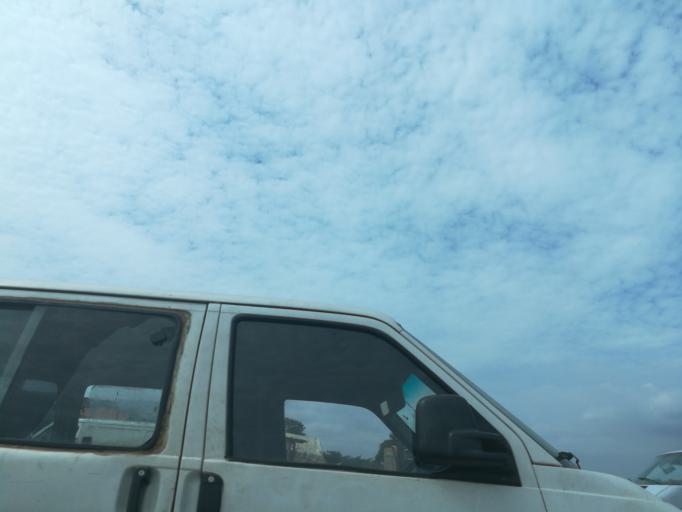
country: NG
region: Lagos
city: Oshodi
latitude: 6.5598
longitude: 3.3225
